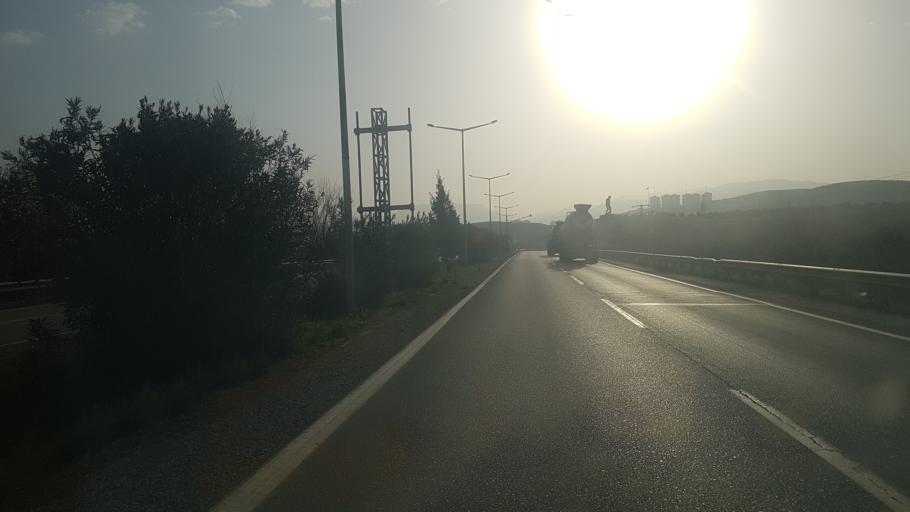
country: TR
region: Osmaniye
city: Toprakkale
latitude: 37.0530
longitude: 36.1460
